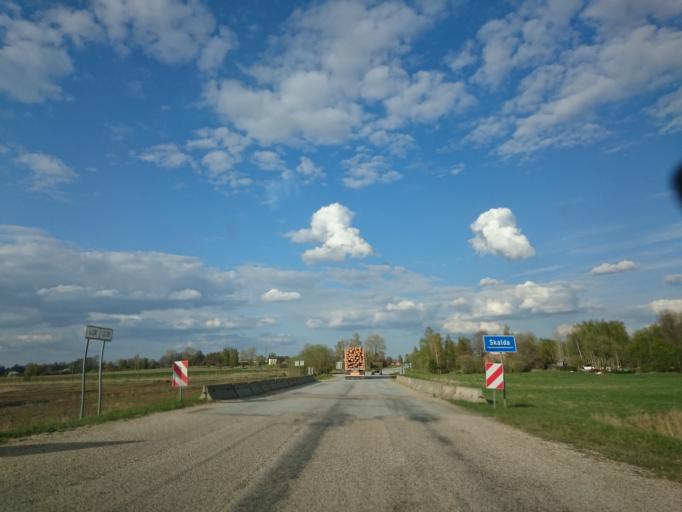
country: LV
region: Aizpute
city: Aizpute
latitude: 56.7935
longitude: 21.6599
